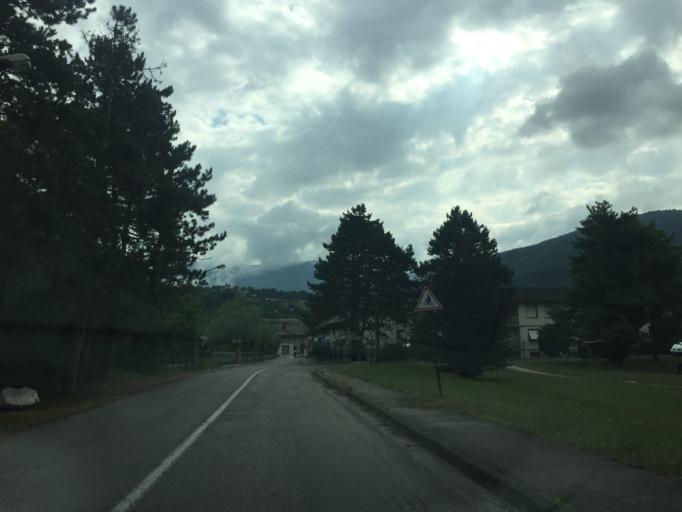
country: FR
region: Rhone-Alpes
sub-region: Departement de la Savoie
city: La Ravoire
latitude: 45.5742
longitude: 5.9677
